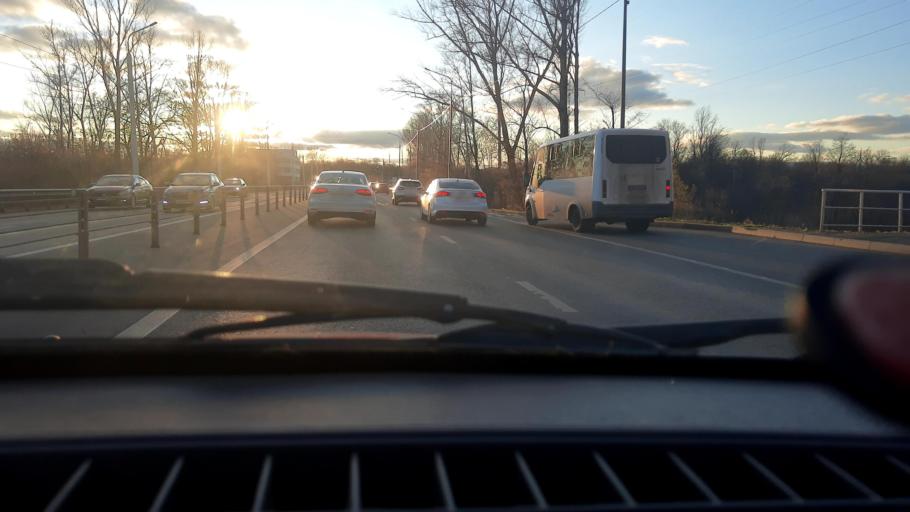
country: RU
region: Bashkortostan
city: Ufa
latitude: 54.6995
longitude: 55.9014
